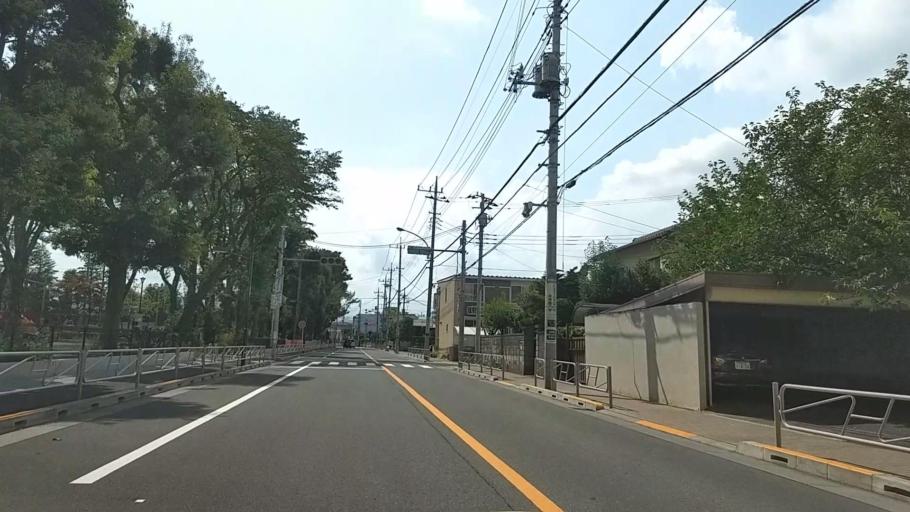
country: JP
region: Tokyo
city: Hachioji
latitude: 35.6532
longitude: 139.3234
